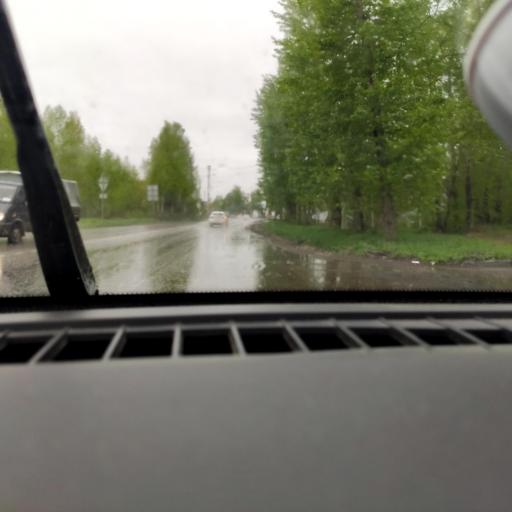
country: RU
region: Perm
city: Perm
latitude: 58.1103
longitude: 56.3230
